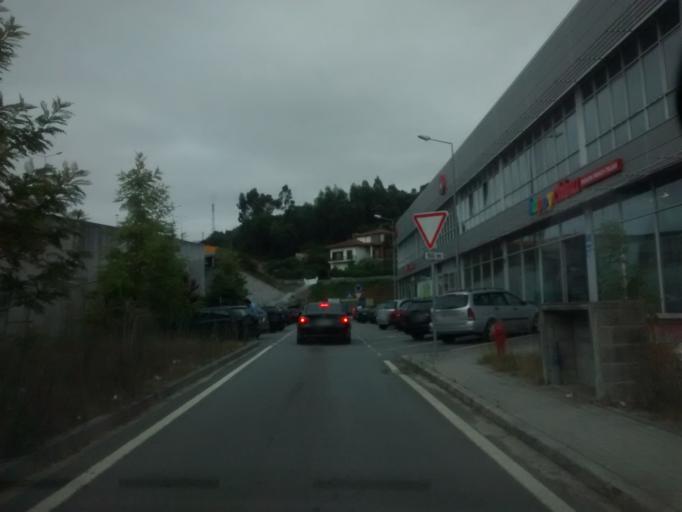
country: PT
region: Braga
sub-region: Braga
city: Braga
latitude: 41.5631
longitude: -8.4072
